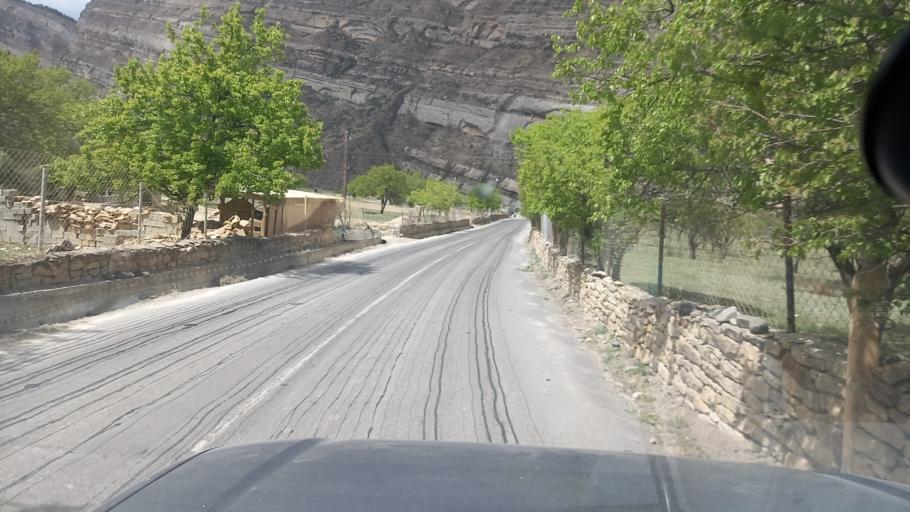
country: RU
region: Dagestan
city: Gunib
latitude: 42.3174
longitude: 46.9237
